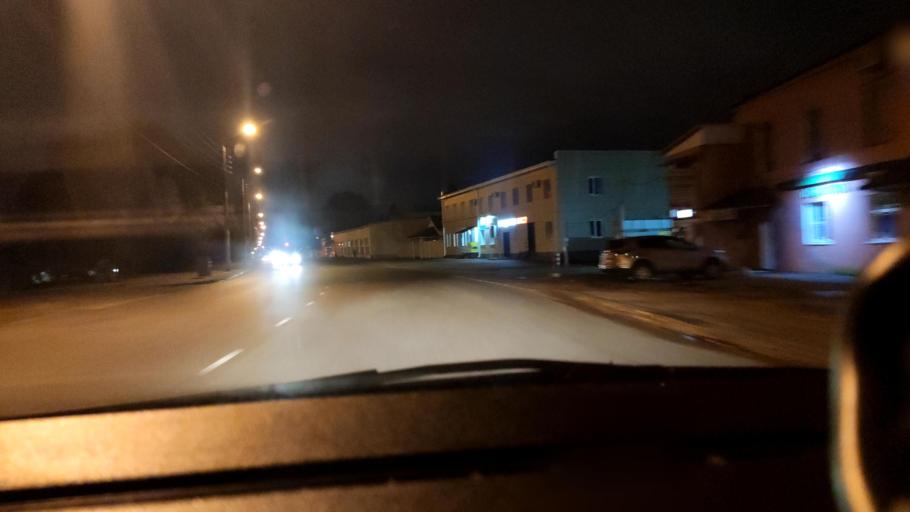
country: RU
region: Voronezj
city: Voronezh
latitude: 51.6256
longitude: 39.1766
